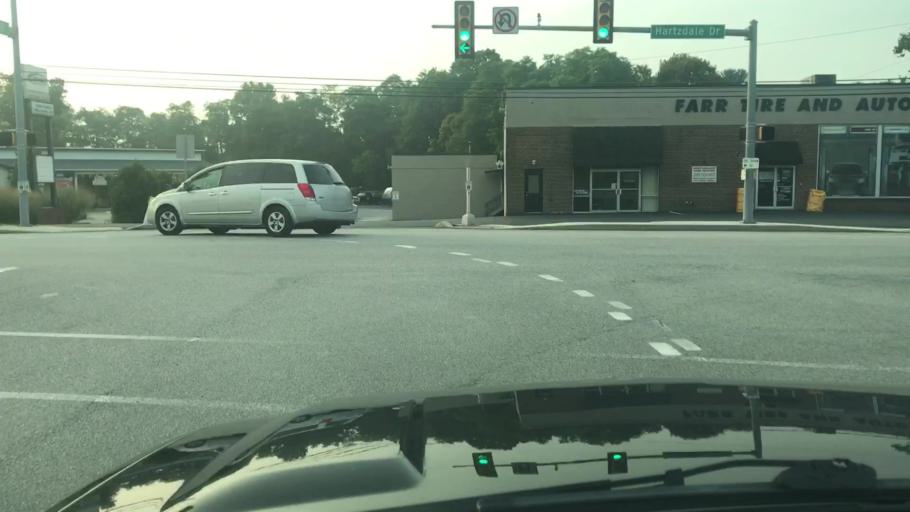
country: US
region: Pennsylvania
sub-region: Cumberland County
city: Shiremanstown
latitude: 40.2201
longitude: -76.9345
